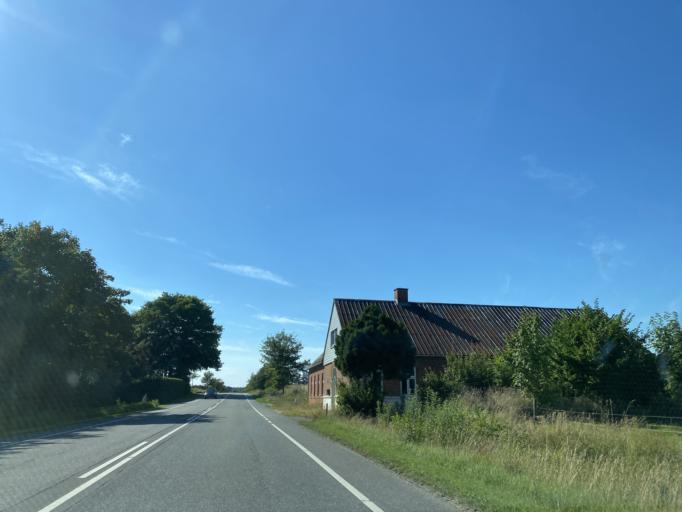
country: DK
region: Central Jutland
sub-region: Hedensted Kommune
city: Torring
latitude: 55.8661
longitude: 9.3876
